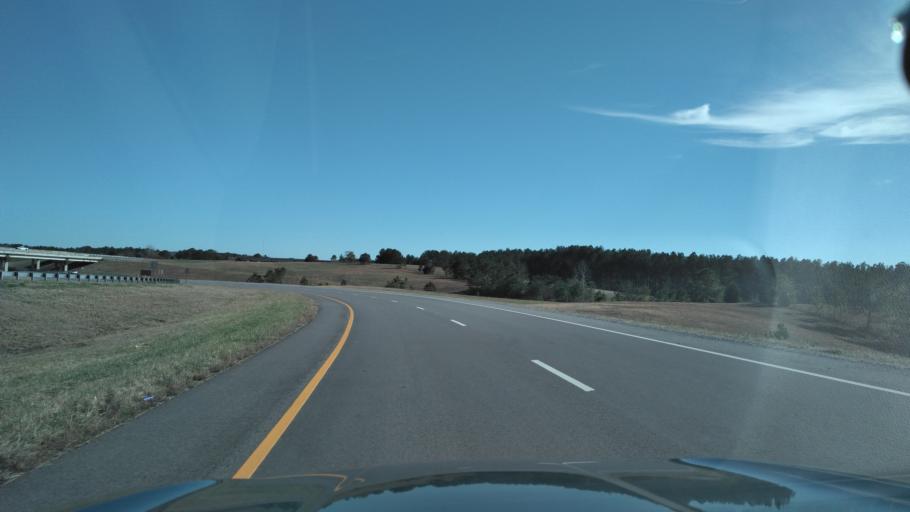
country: US
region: Alabama
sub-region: Walker County
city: Jasper
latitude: 33.8542
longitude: -87.3502
